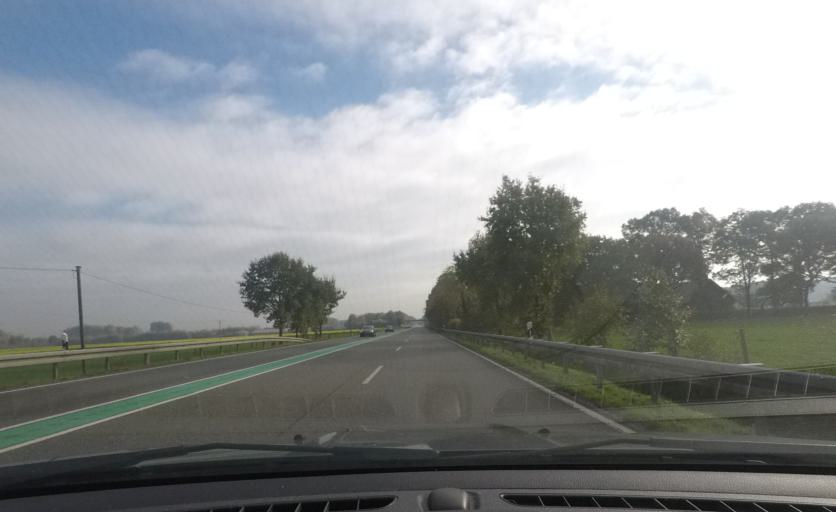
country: DE
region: North Rhine-Westphalia
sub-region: Regierungsbezirk Munster
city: Velen
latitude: 51.8533
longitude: 7.0148
